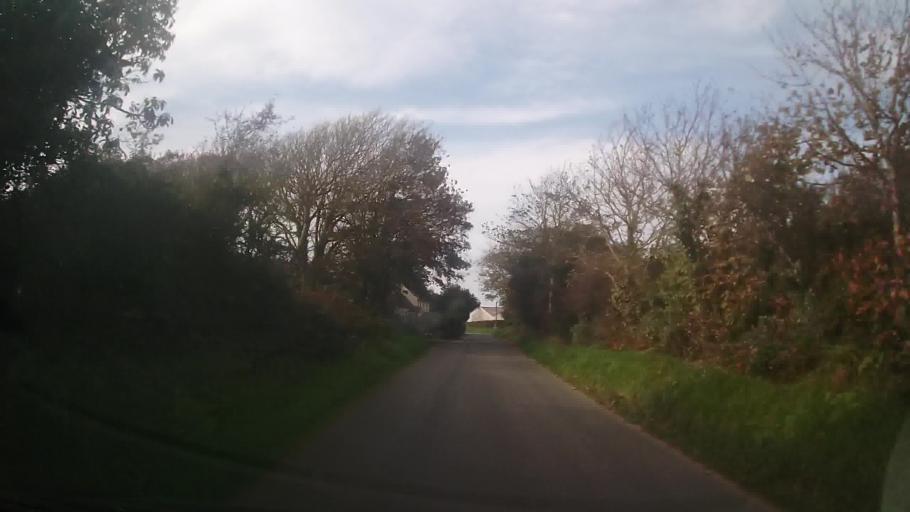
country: GB
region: Wales
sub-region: Pembrokeshire
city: Camrose
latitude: 51.8803
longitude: -5.0484
